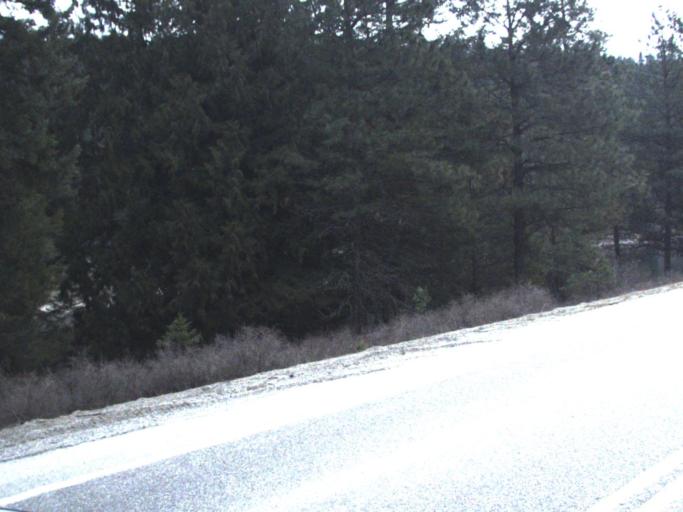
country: US
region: Washington
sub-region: Pend Oreille County
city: Newport
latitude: 48.5417
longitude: -117.3061
